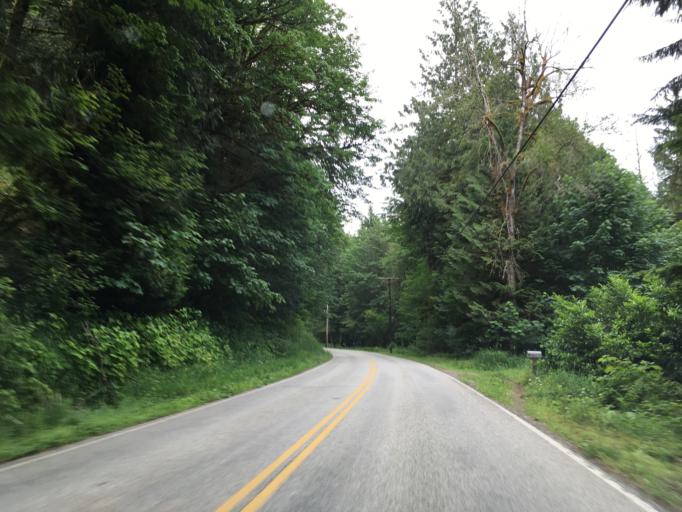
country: US
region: Washington
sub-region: Whatcom County
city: Peaceful Valley
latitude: 48.9318
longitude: -122.0717
